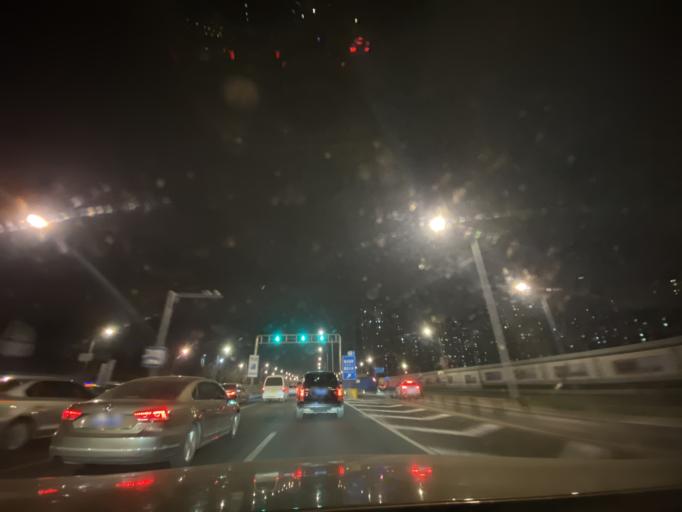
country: CN
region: Beijing
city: Babaoshan
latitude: 39.8958
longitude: 116.2399
